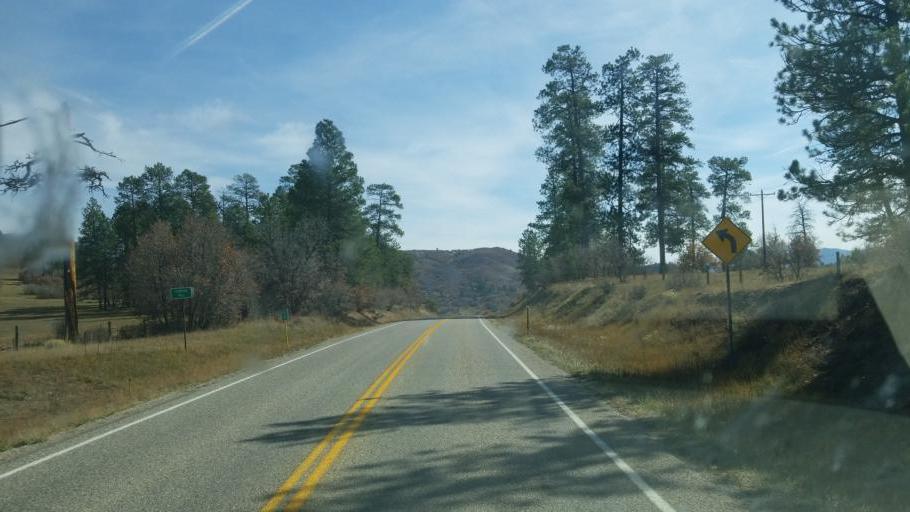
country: US
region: New Mexico
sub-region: Rio Arriba County
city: Dulce
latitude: 37.0746
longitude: -106.8362
